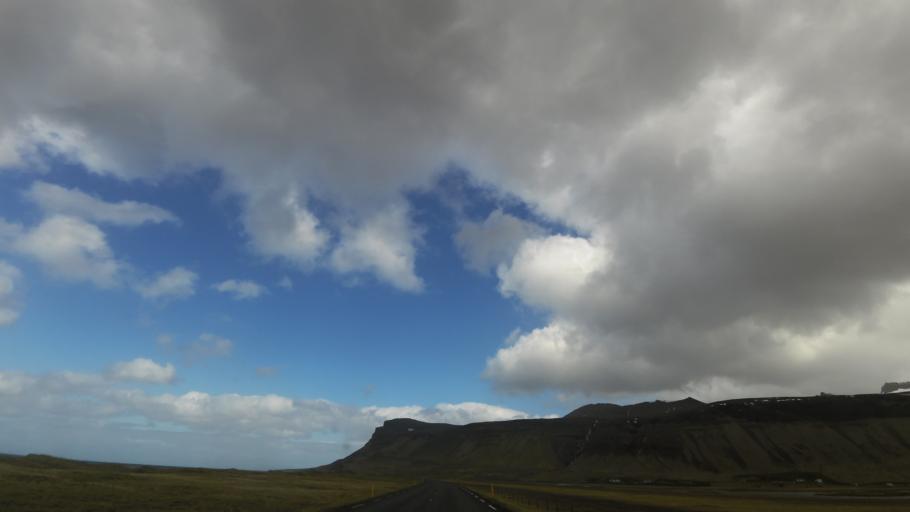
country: IS
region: West
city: Olafsvik
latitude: 64.9210
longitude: -23.5185
